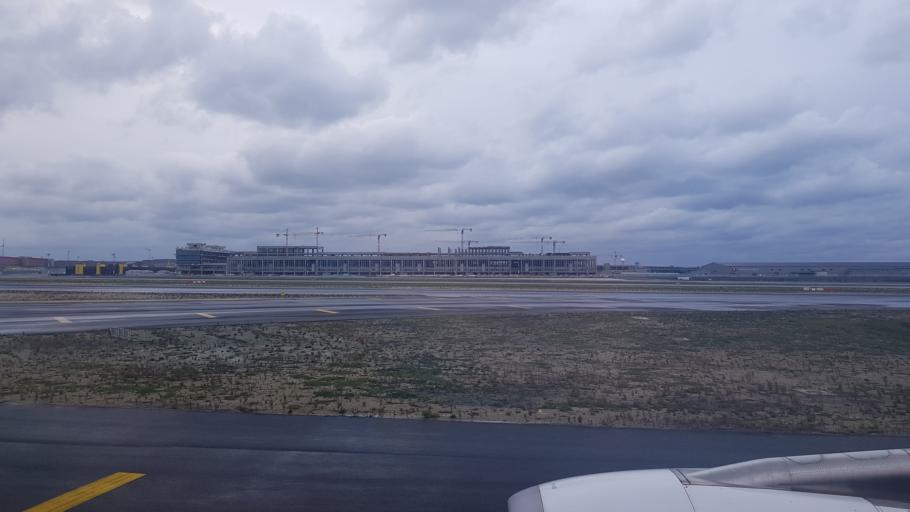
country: TR
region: Istanbul
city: Durusu
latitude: 41.2779
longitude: 28.7296
